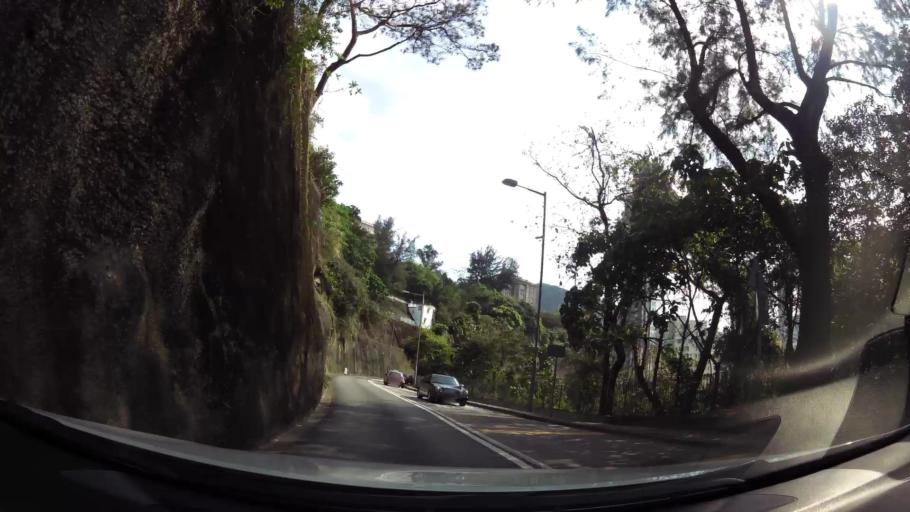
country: HK
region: Wanchai
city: Wan Chai
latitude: 22.2703
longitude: 114.1911
